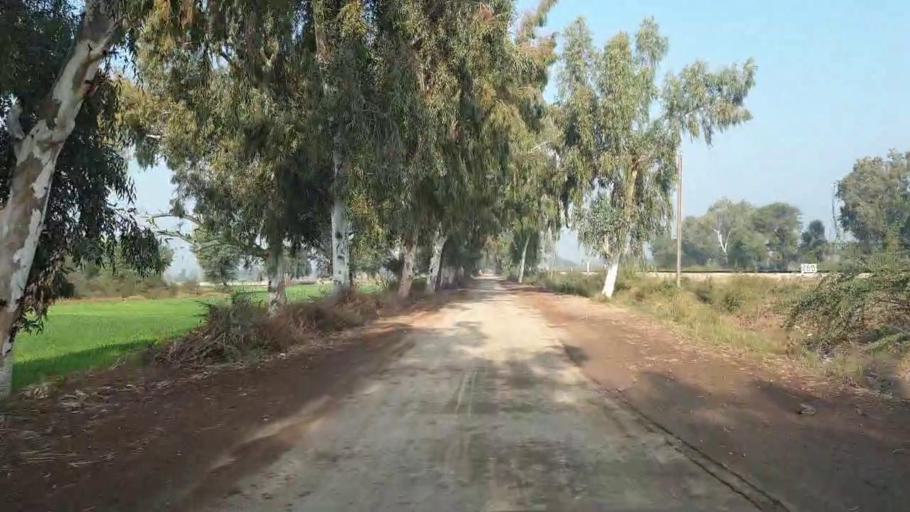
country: PK
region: Sindh
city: Shahdadpur
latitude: 25.9658
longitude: 68.6108
